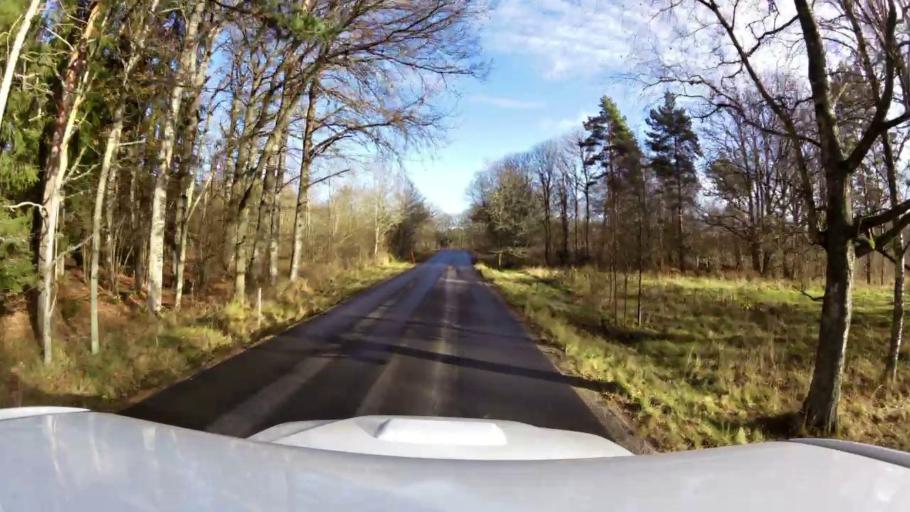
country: SE
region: OEstergoetland
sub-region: Linkopings Kommun
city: Linkoping
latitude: 58.3790
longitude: 15.6268
